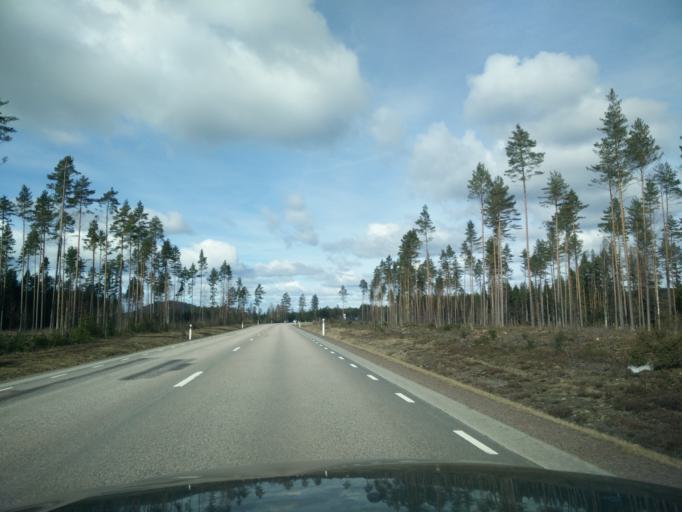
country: SE
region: Vaermland
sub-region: Hagfors Kommun
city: Hagfors
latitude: 60.0183
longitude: 13.5930
